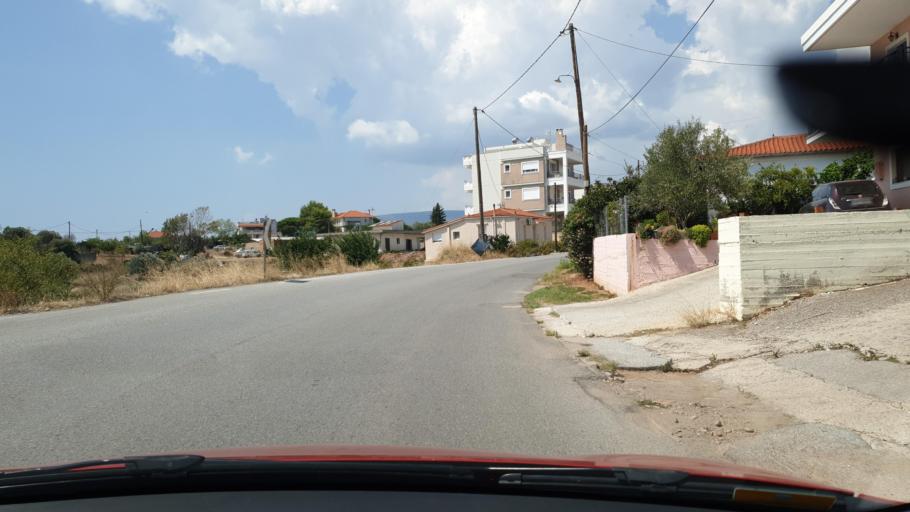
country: GR
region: Central Greece
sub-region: Nomos Evvoias
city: Aliveri
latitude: 38.4027
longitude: 24.0484
